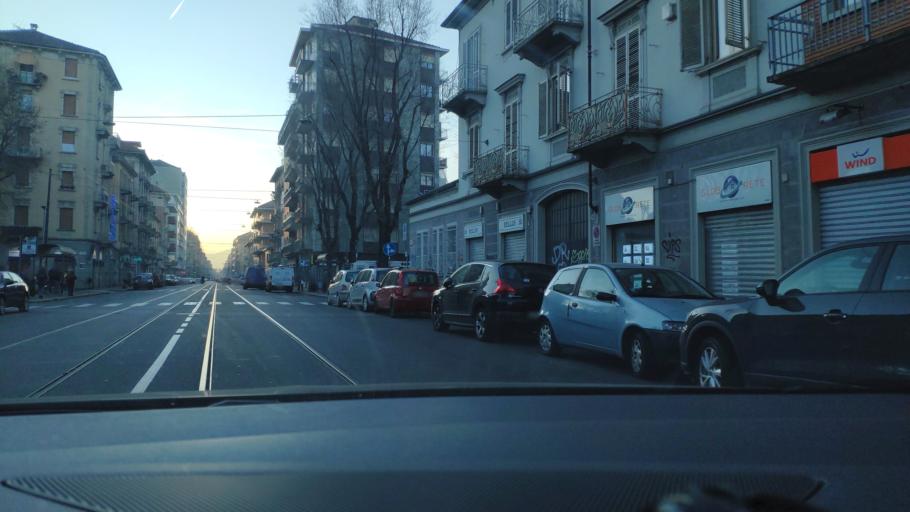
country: IT
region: Piedmont
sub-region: Provincia di Torino
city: Turin
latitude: 45.0827
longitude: 7.6525
